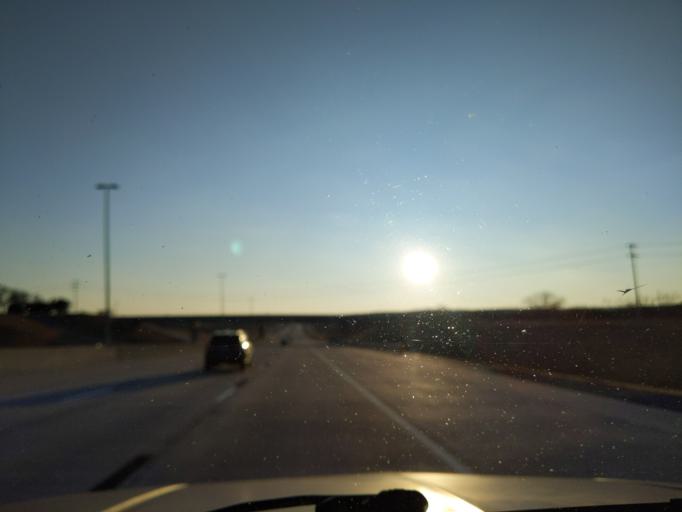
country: US
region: Oklahoma
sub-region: Creek County
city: Kellyville
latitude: 35.9264
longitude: -96.2782
